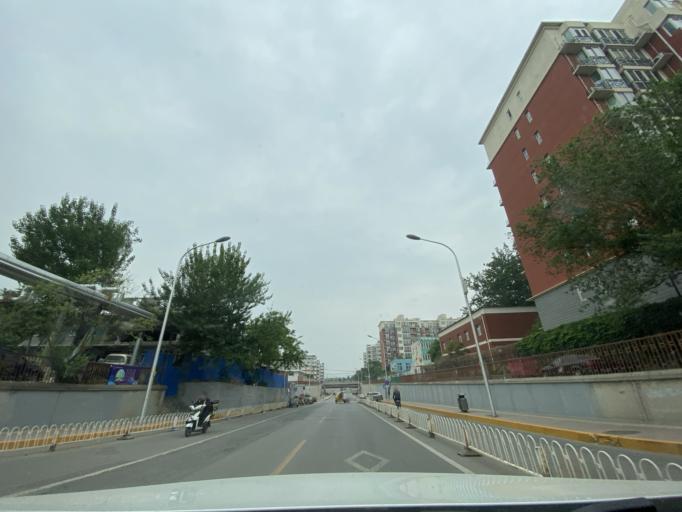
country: CN
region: Beijing
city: Babaoshan
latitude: 39.9295
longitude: 116.2422
